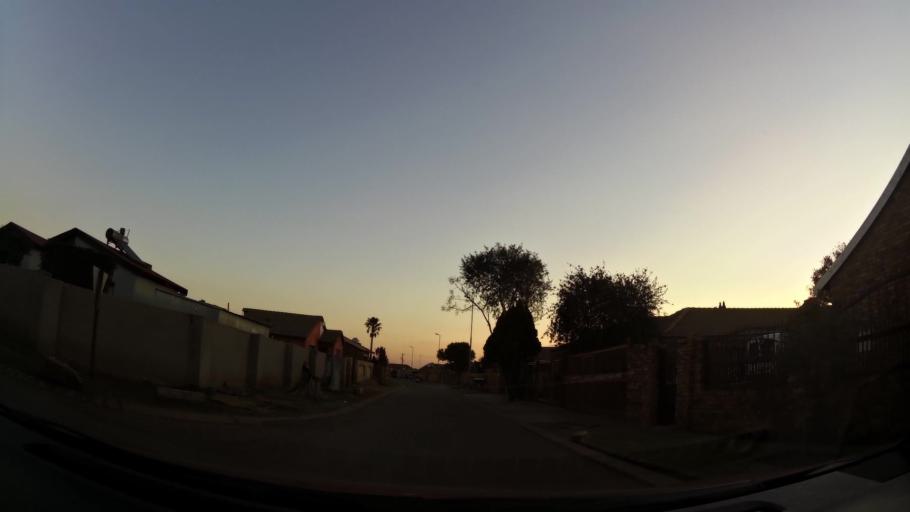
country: ZA
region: Gauteng
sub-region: City of Johannesburg Metropolitan Municipality
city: Soweto
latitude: -26.2264
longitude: 27.8405
